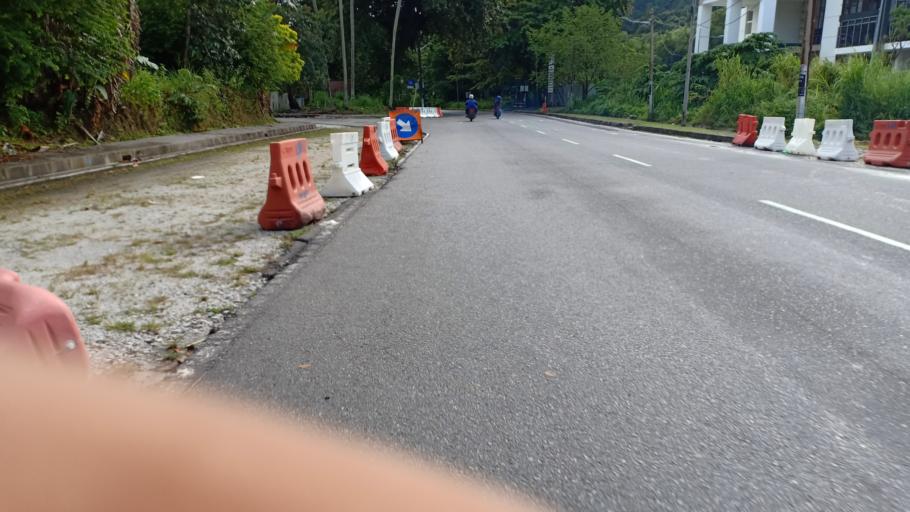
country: MY
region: Penang
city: Tanjung Tokong
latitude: 5.4594
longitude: 100.2171
